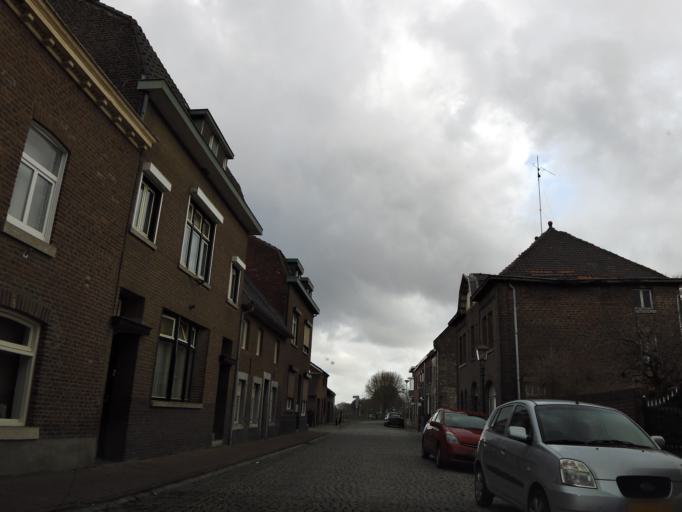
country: NL
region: Limburg
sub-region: Eijsden-Margraten
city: Eijsden
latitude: 50.7779
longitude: 5.7007
